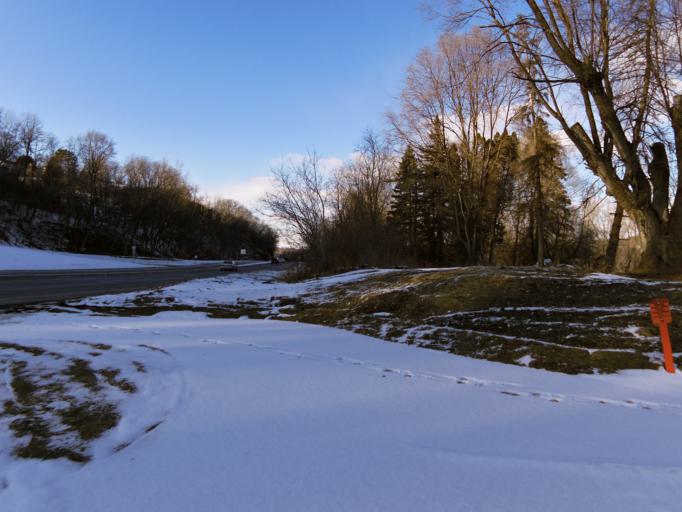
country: US
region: Minnesota
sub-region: Washington County
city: Oak Park Heights
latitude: 45.0434
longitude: -92.7954
